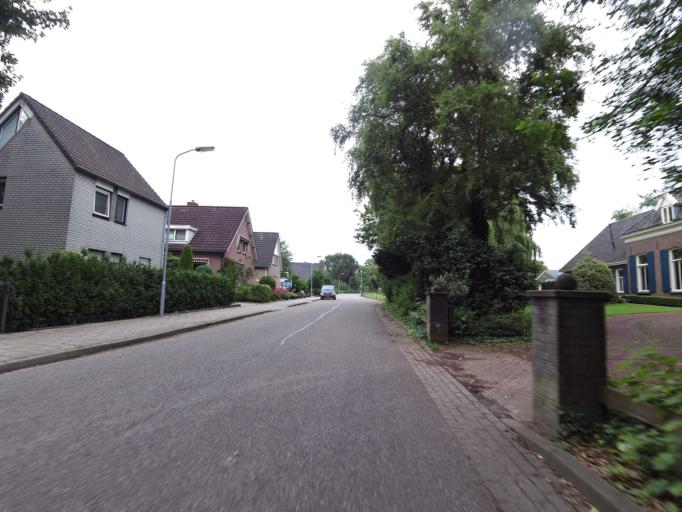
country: NL
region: Gelderland
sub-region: Gemeente Doesburg
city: Doesburg
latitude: 51.9954
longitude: 6.1372
